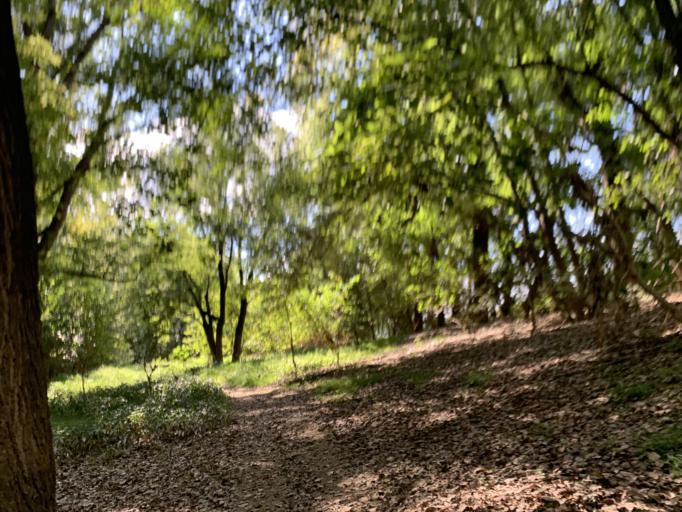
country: US
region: Indiana
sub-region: Floyd County
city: New Albany
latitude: 38.2756
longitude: -85.8220
